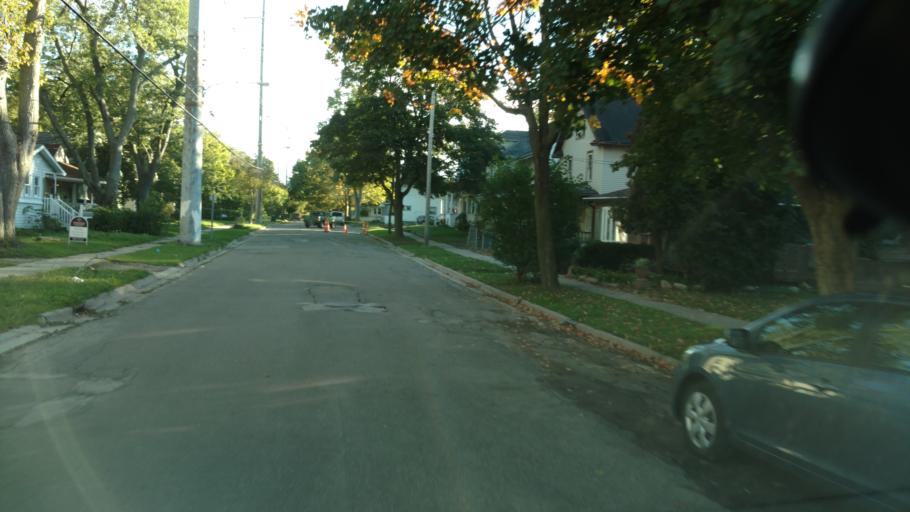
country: US
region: Michigan
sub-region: Ingham County
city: Lansing
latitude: 42.7294
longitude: -84.5213
